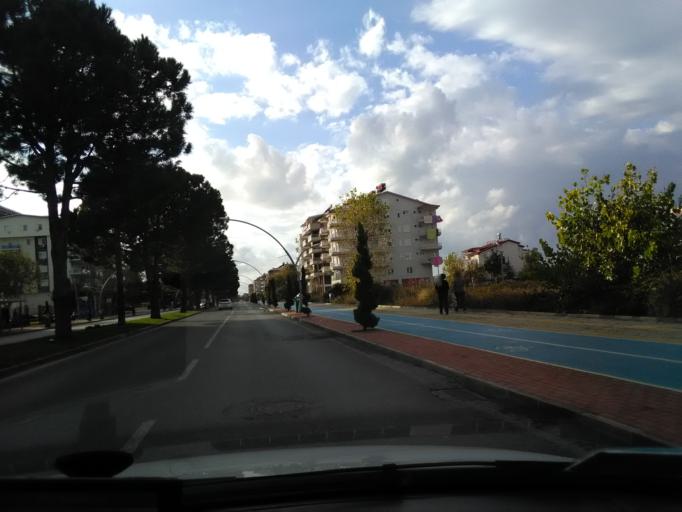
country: TR
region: Antalya
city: Gazipasa
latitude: 36.2658
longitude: 32.2953
